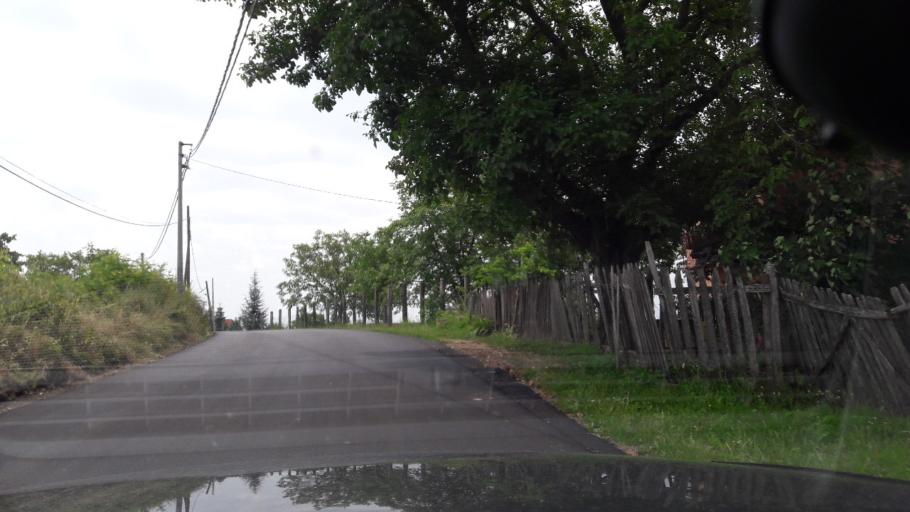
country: RS
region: Central Serbia
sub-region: Belgrade
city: Sopot
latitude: 44.6033
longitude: 20.6012
